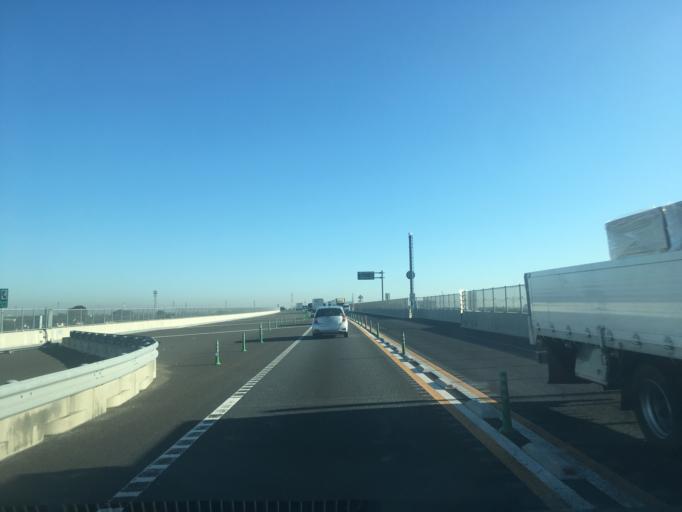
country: JP
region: Saitama
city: Kukichuo
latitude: 36.0577
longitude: 139.6953
